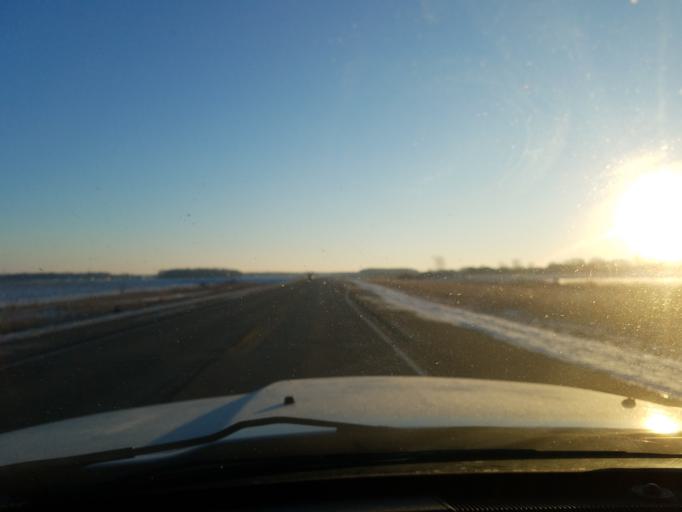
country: US
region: Indiana
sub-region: Marshall County
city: Bremen
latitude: 41.4607
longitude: -86.1495
